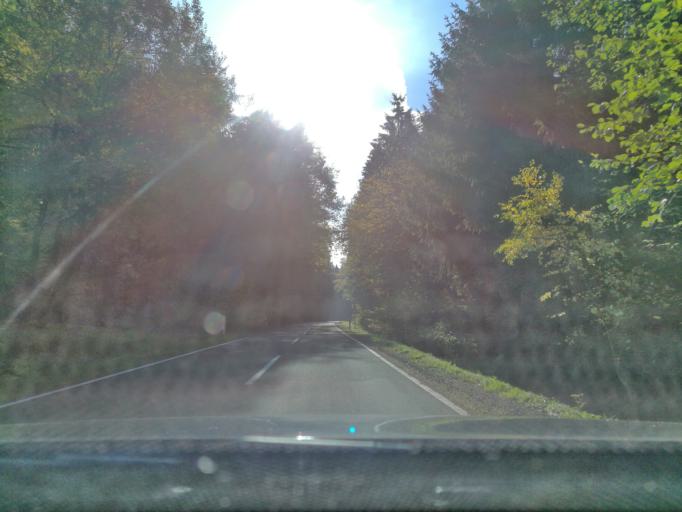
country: DE
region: Hesse
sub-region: Regierungsbezirk Kassel
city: Poppenhausen
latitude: 50.4662
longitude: 9.8761
